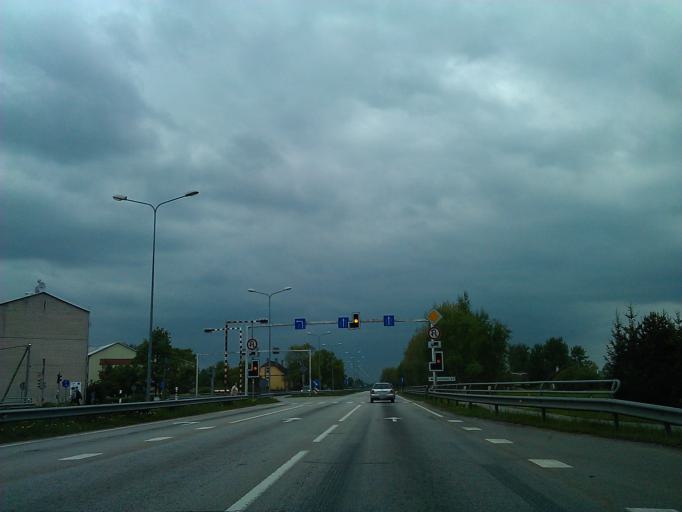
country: LV
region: Olaine
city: Olaine
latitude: 56.8024
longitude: 23.9847
